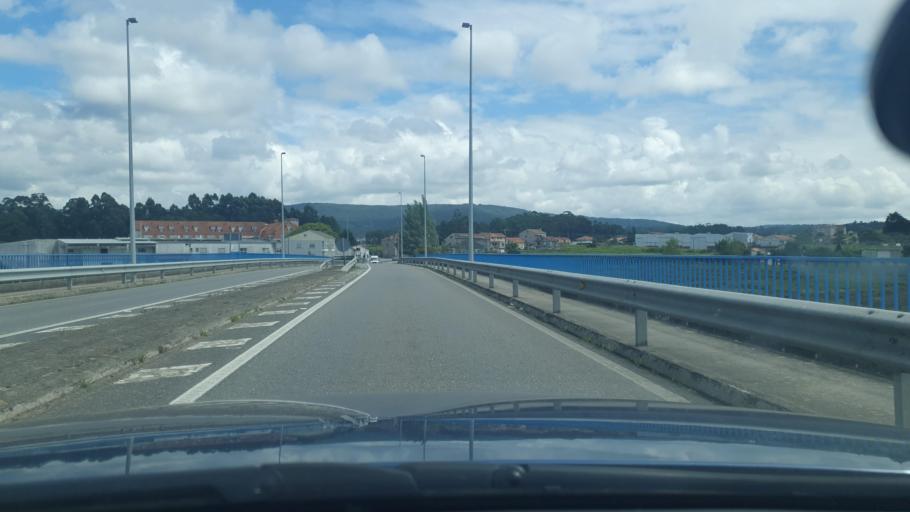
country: ES
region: Galicia
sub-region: Provincia de Pontevedra
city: Cambados
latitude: 42.5015
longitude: -8.8058
